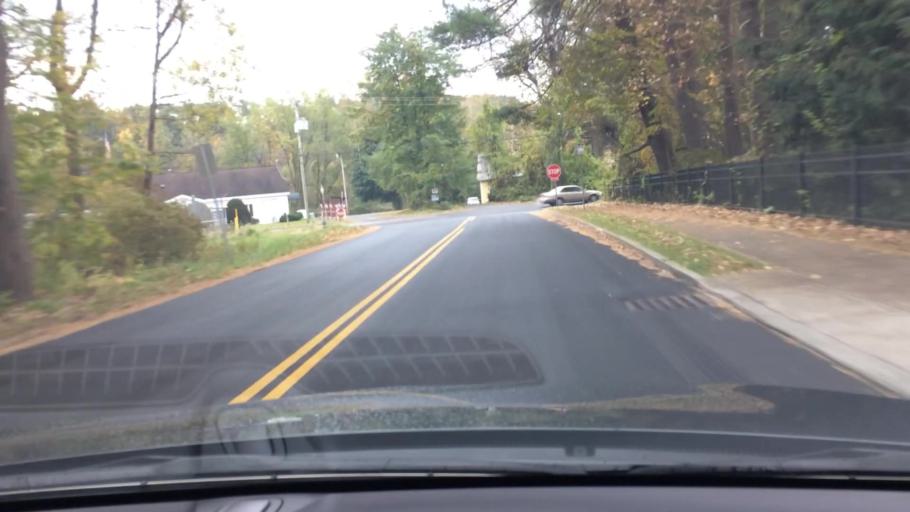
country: US
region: New York
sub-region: Saratoga County
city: Saratoga Springs
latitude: 43.0913
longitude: -73.7626
